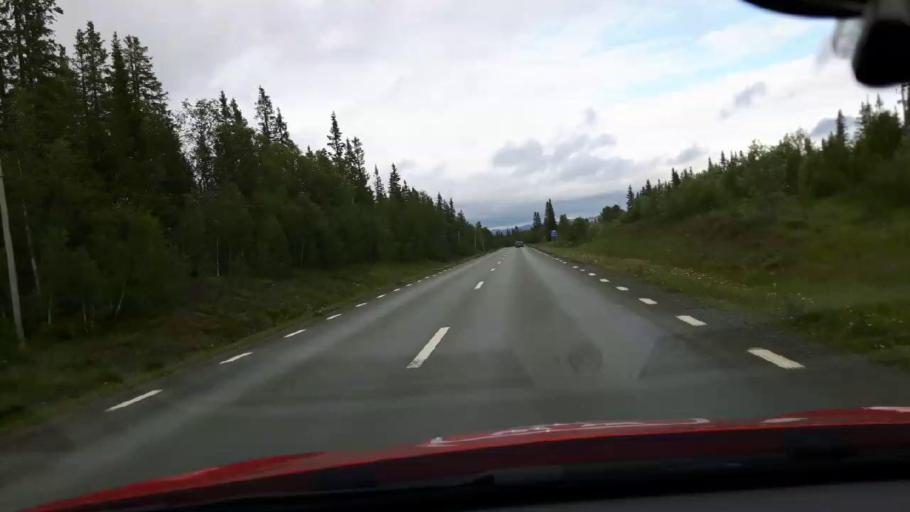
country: SE
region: Jaemtland
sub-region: Are Kommun
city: Are
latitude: 63.3096
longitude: 12.4675
